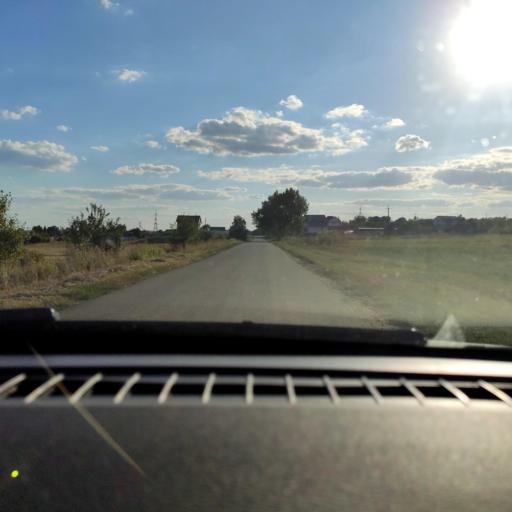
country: RU
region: Voronezj
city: Devitsa
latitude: 51.6482
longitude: 38.9518
